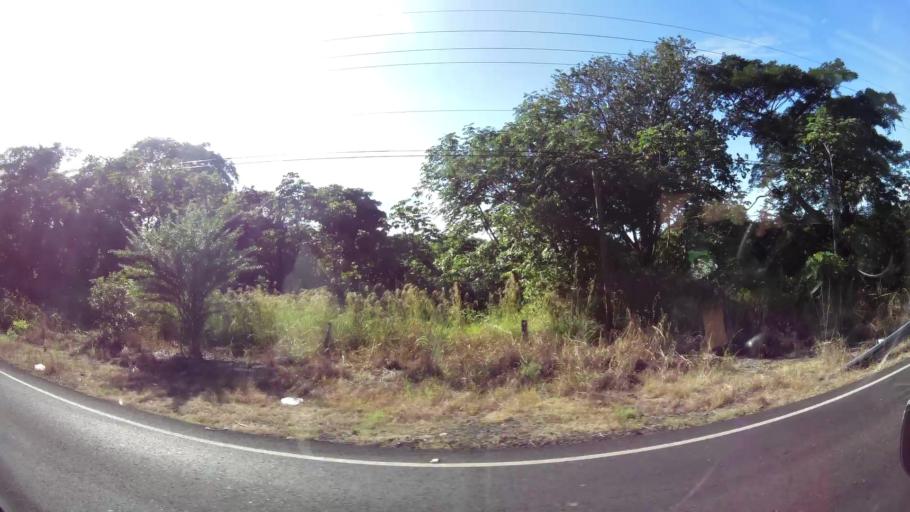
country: CR
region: Guanacaste
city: Sardinal
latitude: 10.5863
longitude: -85.6372
